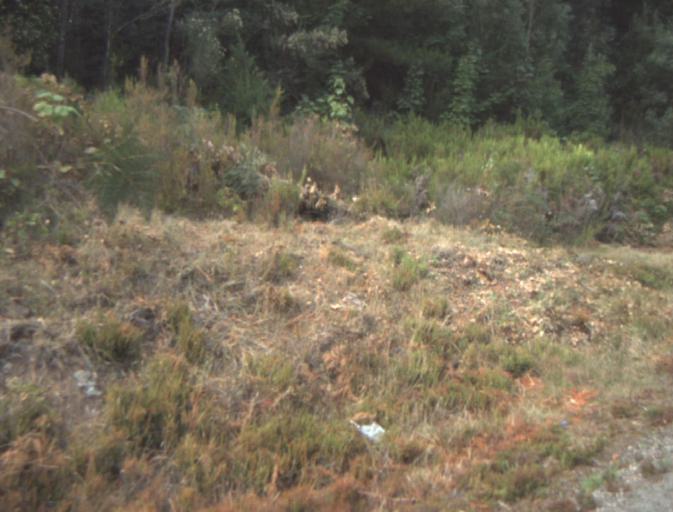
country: AU
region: Tasmania
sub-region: Launceston
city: Mayfield
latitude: -41.3030
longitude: 147.2052
